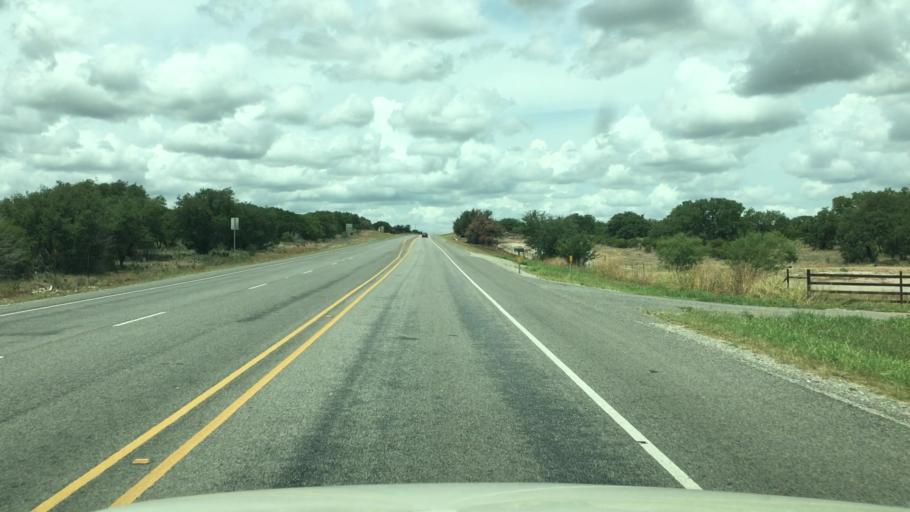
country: US
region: Texas
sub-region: McCulloch County
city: Brady
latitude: 31.0302
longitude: -99.2290
